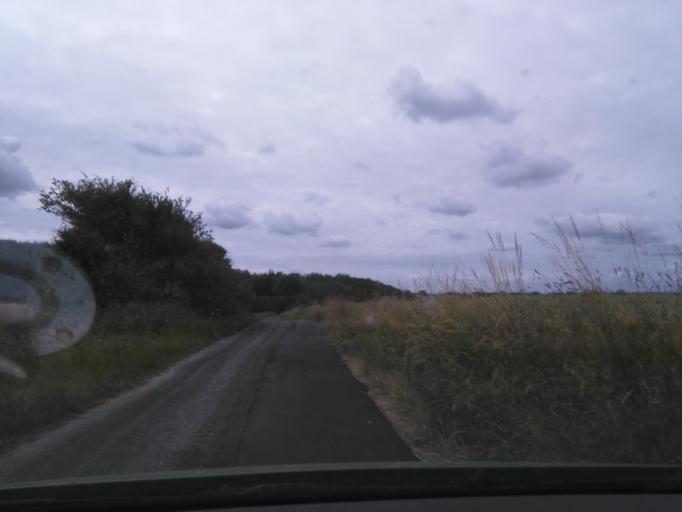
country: DK
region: Central Jutland
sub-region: Arhus Kommune
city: Solbjerg
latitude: 55.9988
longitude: 10.0527
